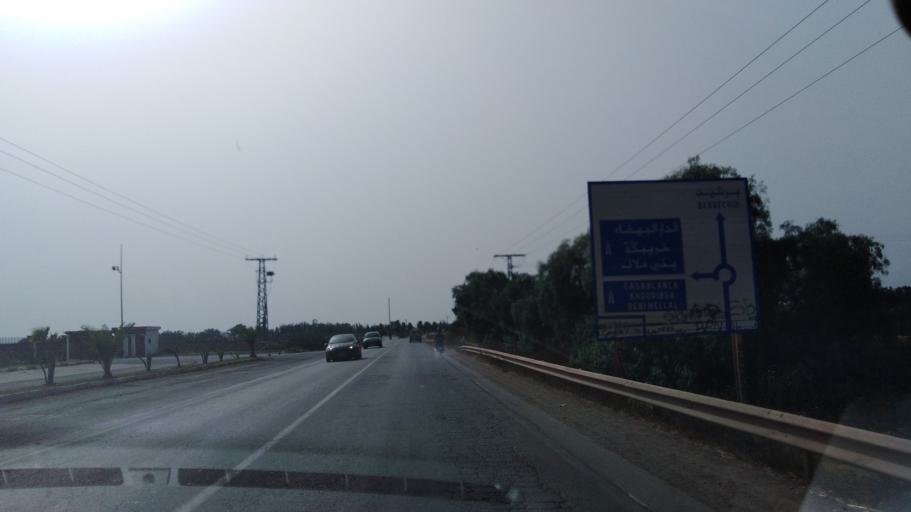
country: MA
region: Chaouia-Ouardigha
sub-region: Settat Province
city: Berrechid
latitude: 33.2466
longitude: -7.5565
